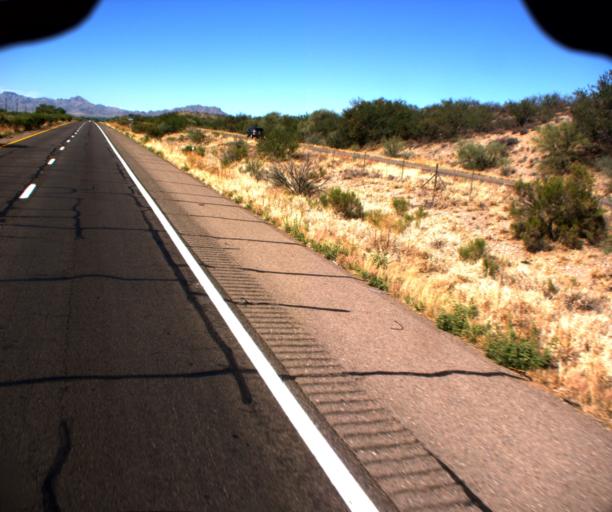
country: US
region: Arizona
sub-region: Pima County
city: Arivaca Junction
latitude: 31.7600
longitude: -111.0391
